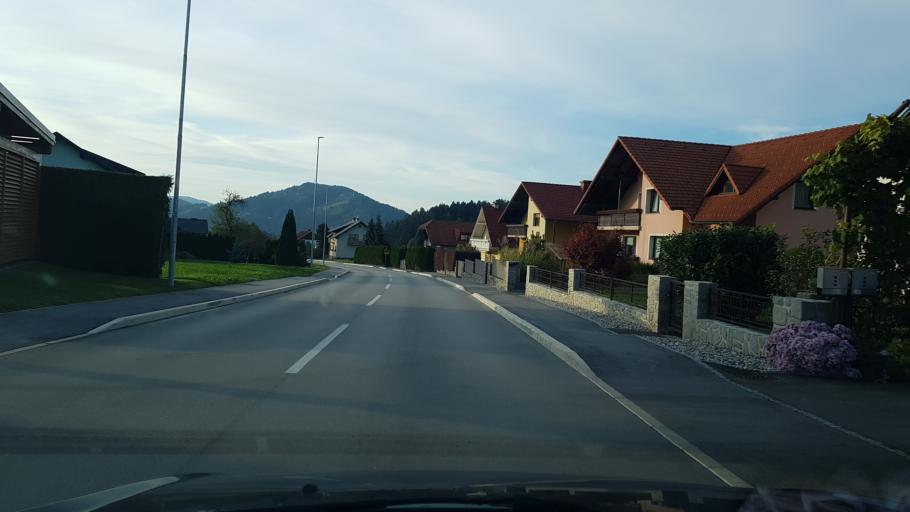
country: SI
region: Slovenj Gradec
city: Smartno pri Slovenj Gradcu
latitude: 46.5029
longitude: 15.1068
